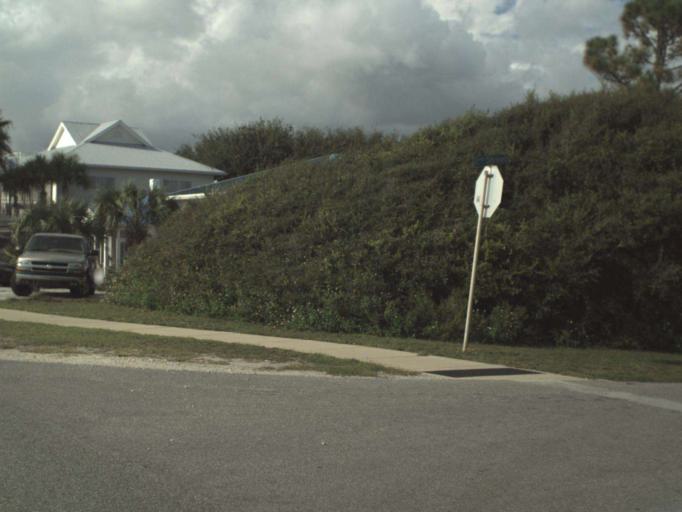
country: US
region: Florida
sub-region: Bay County
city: Mexico Beach
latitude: 29.9304
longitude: -85.3944
